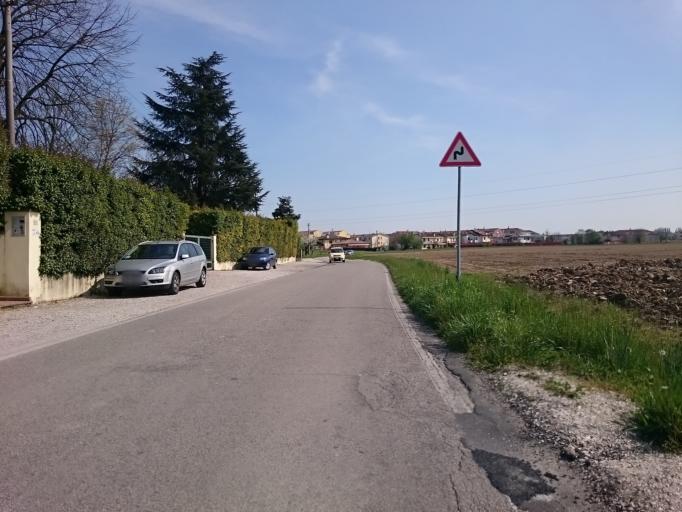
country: IT
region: Veneto
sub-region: Provincia di Padova
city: Rubano
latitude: 45.4343
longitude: 11.7920
